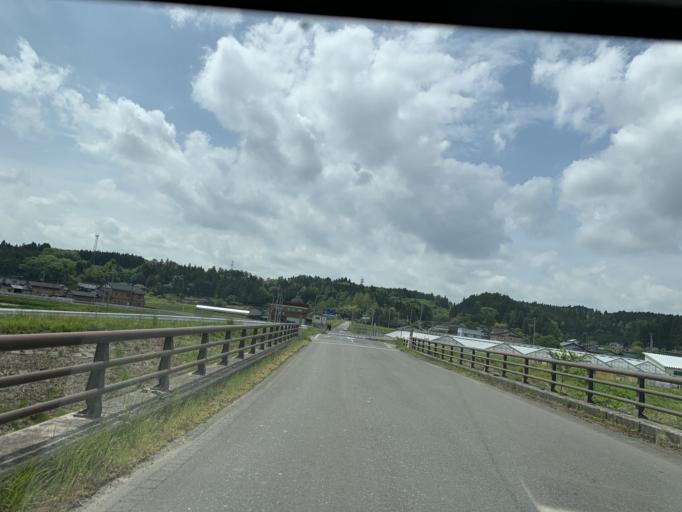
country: JP
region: Miyagi
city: Furukawa
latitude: 38.7426
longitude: 140.9314
